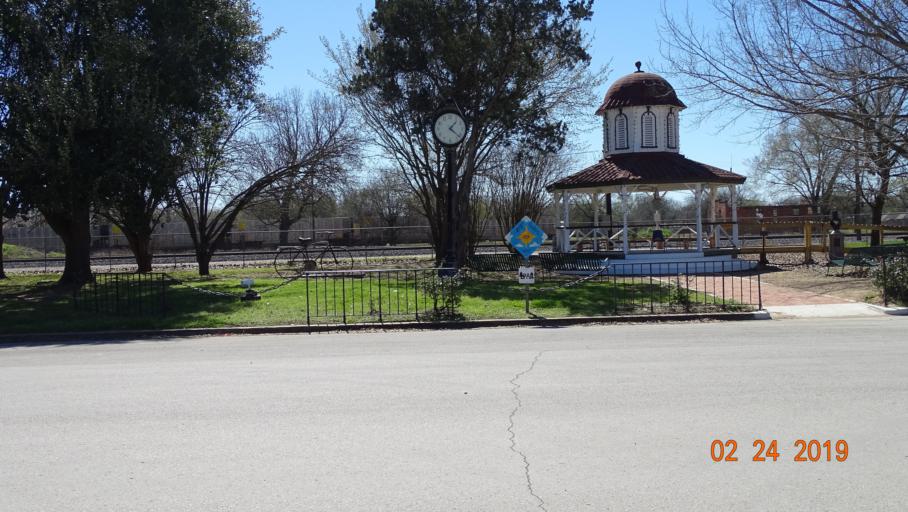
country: US
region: Texas
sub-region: Bastrop County
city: Smithville
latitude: 30.0068
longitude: -97.1605
